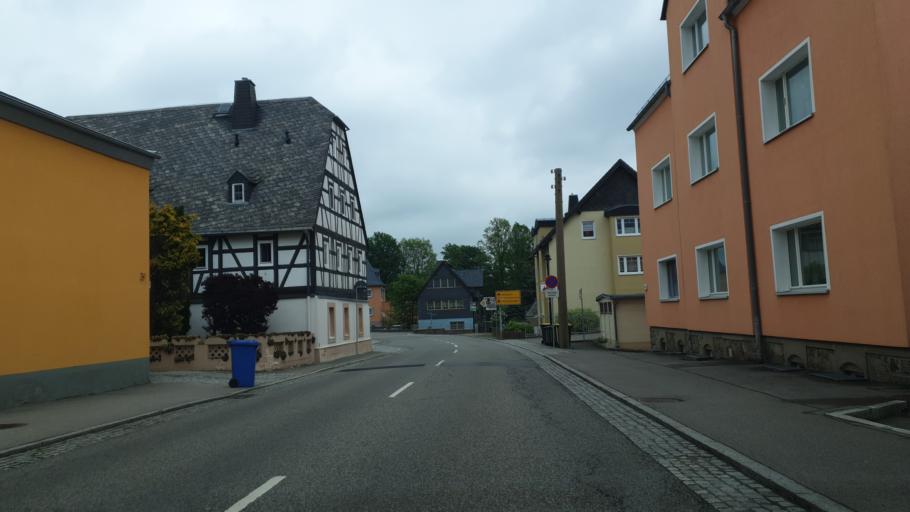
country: DE
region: Saxony
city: Limbach-Oberfrohna
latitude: 50.8564
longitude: 12.7948
